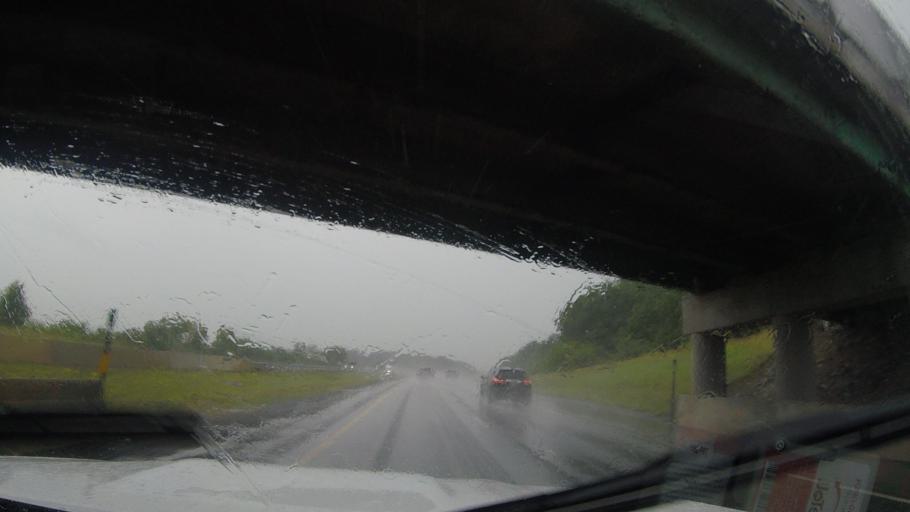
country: US
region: New York
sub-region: Ontario County
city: Phelps
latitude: 42.9679
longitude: -77.0573
